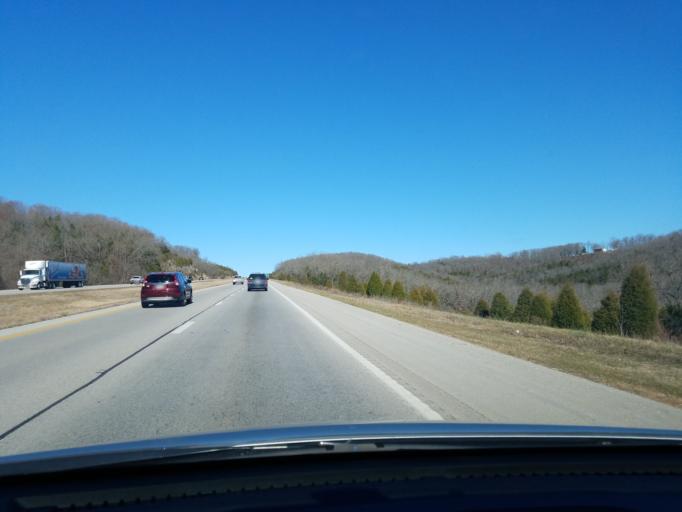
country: US
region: Missouri
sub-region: Taney County
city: Merriam Woods
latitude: 36.7815
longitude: -93.2245
